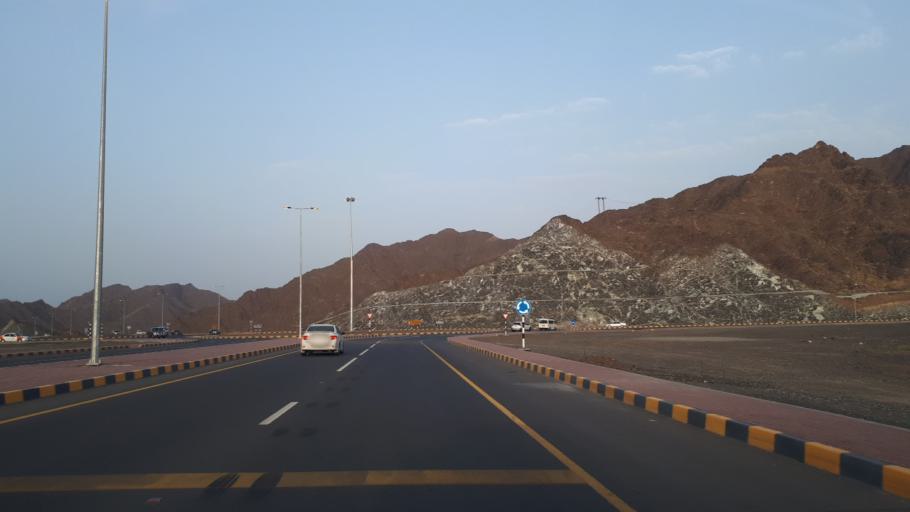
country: OM
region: Al Batinah
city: Rustaq
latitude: 23.4133
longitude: 57.3069
